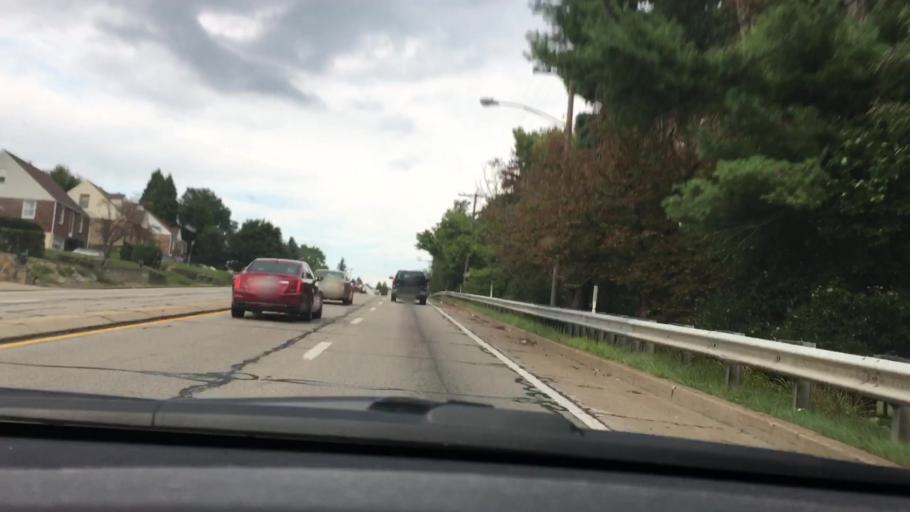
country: US
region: Pennsylvania
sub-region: Allegheny County
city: Baldwin
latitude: 40.3339
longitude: -79.9834
